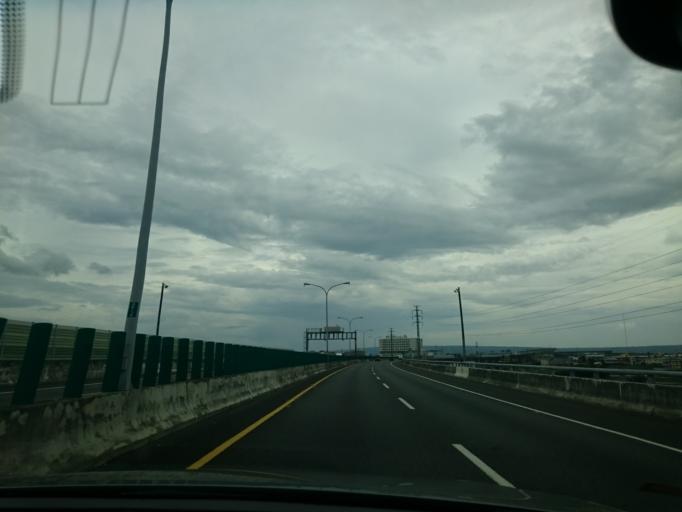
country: TW
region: Taiwan
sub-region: Taichung City
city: Taichung
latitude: 24.0624
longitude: 120.6895
